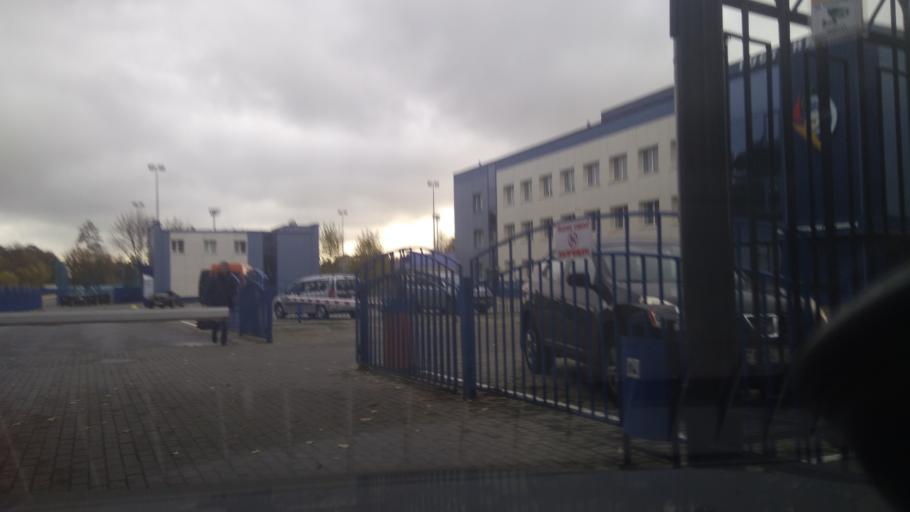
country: BY
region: Minsk
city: Minsk
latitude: 53.9220
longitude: 27.6083
